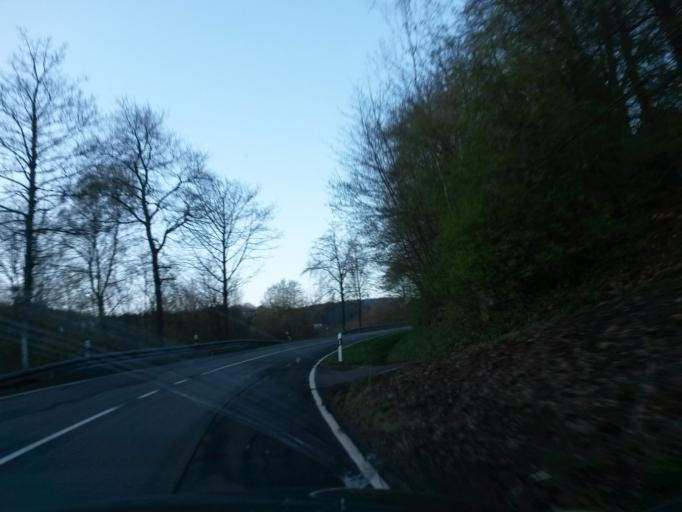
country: DE
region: North Rhine-Westphalia
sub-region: Regierungsbezirk Arnsberg
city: Herscheid
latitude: 51.1682
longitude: 7.7552
